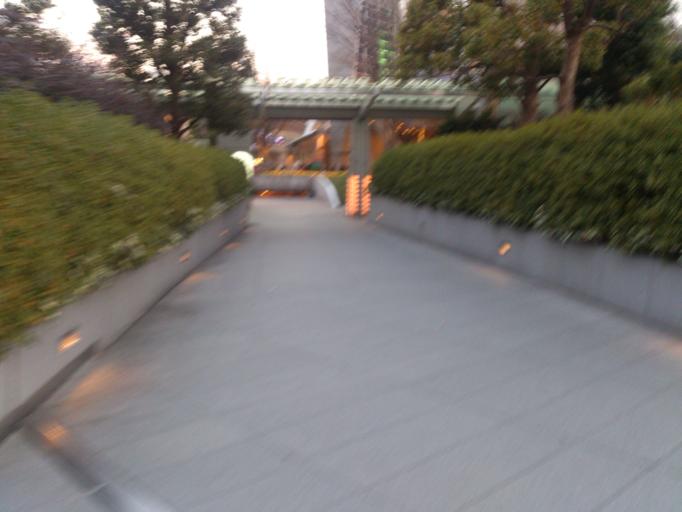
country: JP
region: Tokyo
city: Tokyo
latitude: 35.6616
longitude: 139.7292
